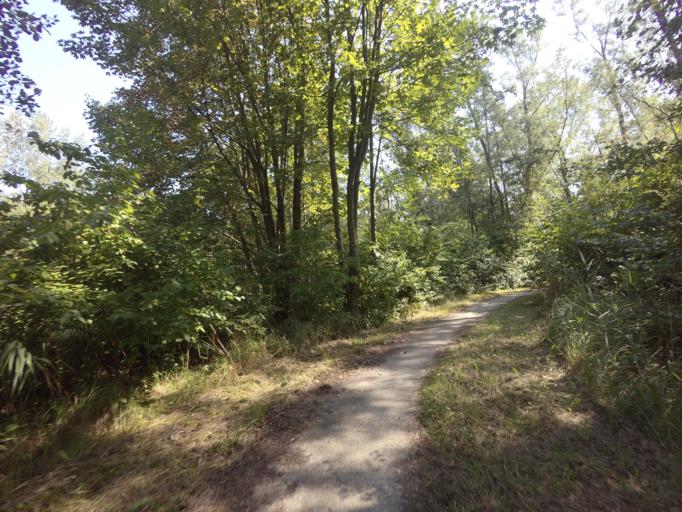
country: NL
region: Groningen
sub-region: Gemeente De Marne
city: Ulrum
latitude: 53.3920
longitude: 6.2650
